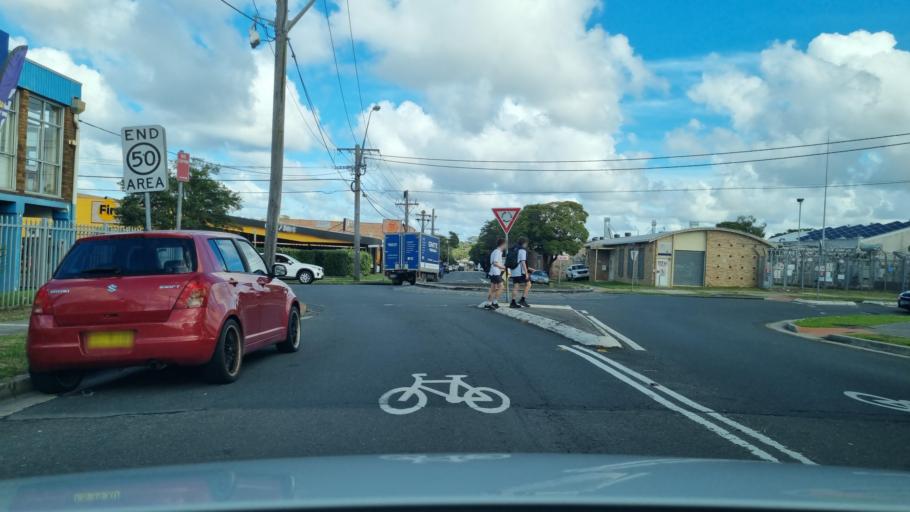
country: AU
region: New South Wales
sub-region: Warringah
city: Brookvale
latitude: -33.7620
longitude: 151.2748
